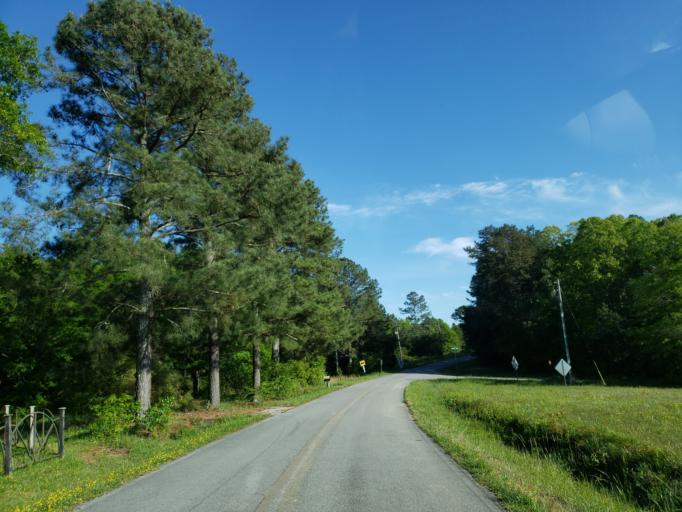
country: US
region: Georgia
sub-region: Polk County
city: Aragon
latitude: 34.0165
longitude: -85.1460
